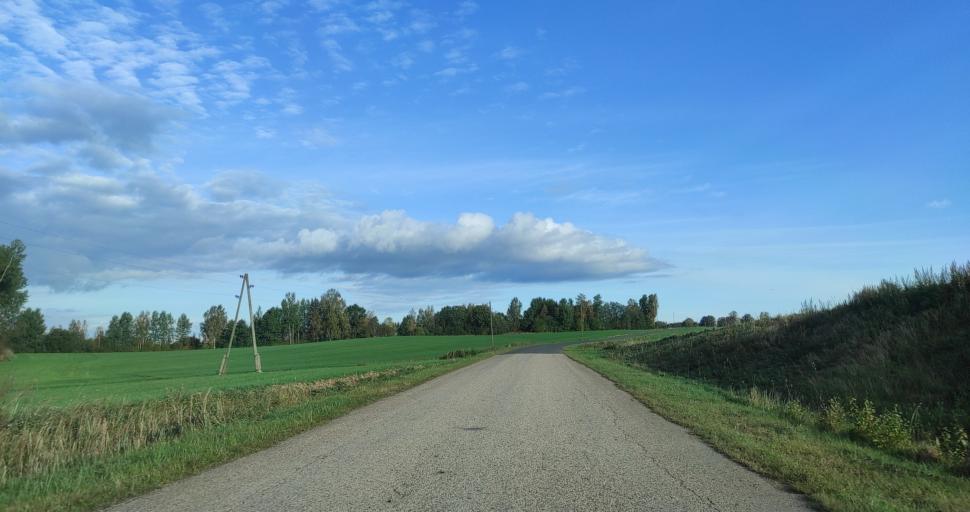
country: LV
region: Aizpute
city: Aizpute
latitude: 56.7611
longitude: 21.7815
